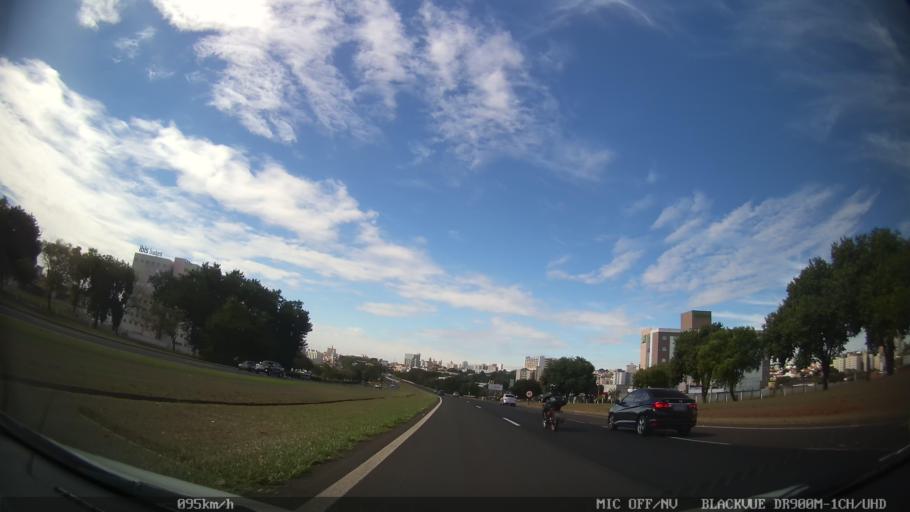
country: BR
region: Sao Paulo
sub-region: Sao Jose Do Rio Preto
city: Sao Jose do Rio Preto
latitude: -20.8252
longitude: -49.4063
